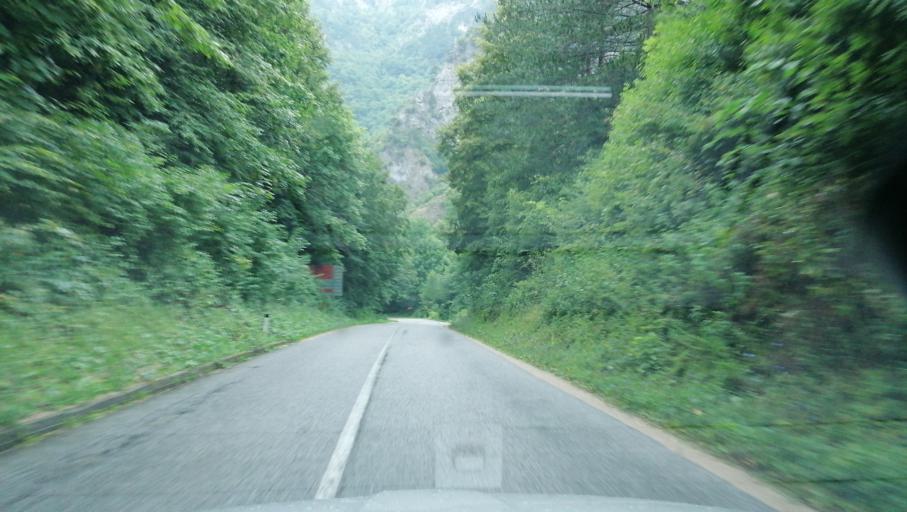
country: BA
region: Republika Srpska
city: Gacko
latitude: 43.3079
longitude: 18.6571
